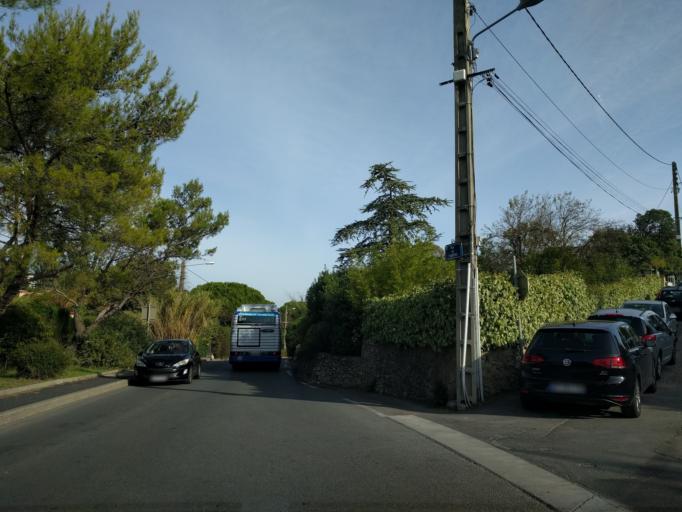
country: FR
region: Languedoc-Roussillon
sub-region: Departement de l'Herault
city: Montferrier-sur-Lez
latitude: 43.6410
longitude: 3.8581
